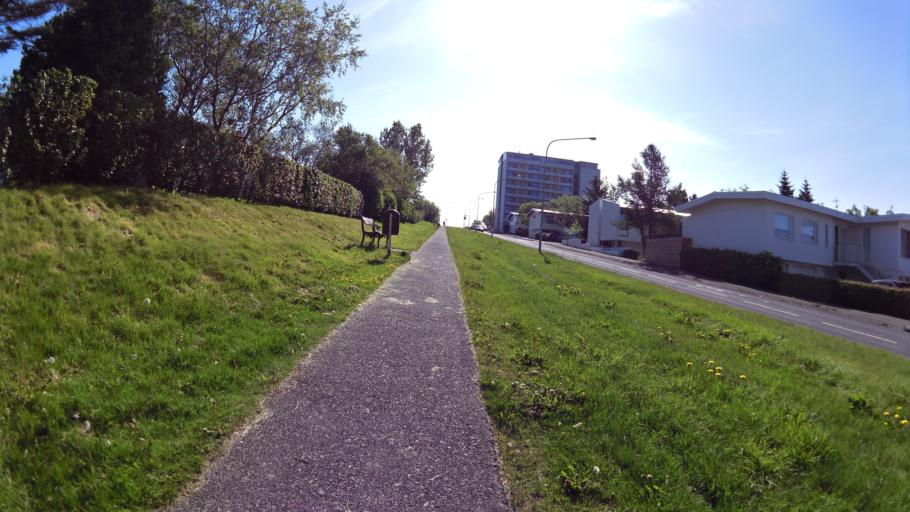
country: IS
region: Capital Region
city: Reykjavik
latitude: 64.1256
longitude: -21.8857
